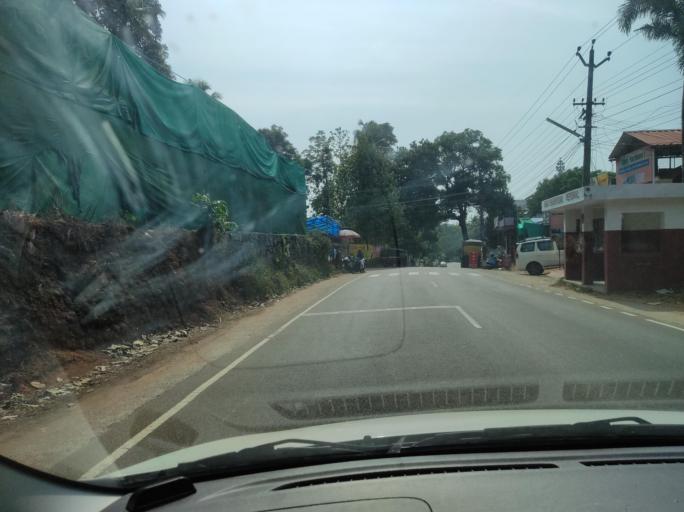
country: IN
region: Kerala
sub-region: Kottayam
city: Kottayam
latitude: 9.6741
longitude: 76.5329
